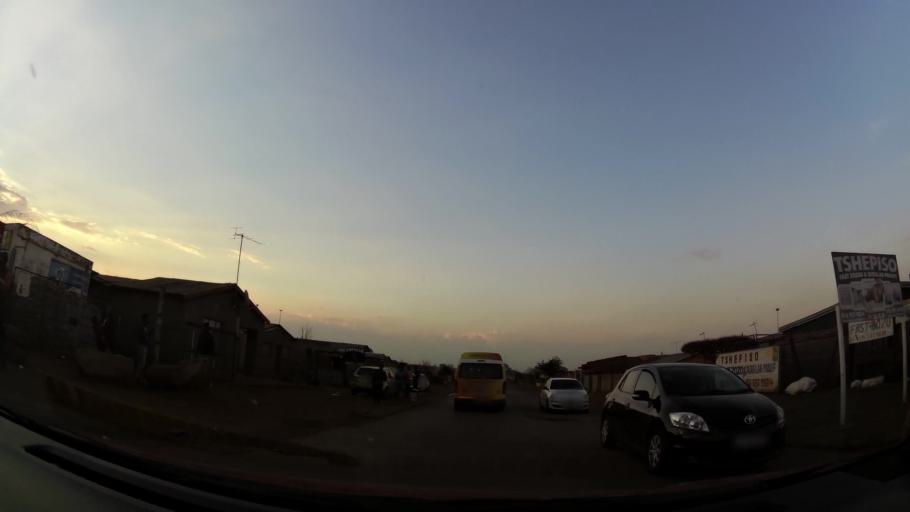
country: ZA
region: Gauteng
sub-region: City of Johannesburg Metropolitan Municipality
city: Orange Farm
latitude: -26.5536
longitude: 27.8633
